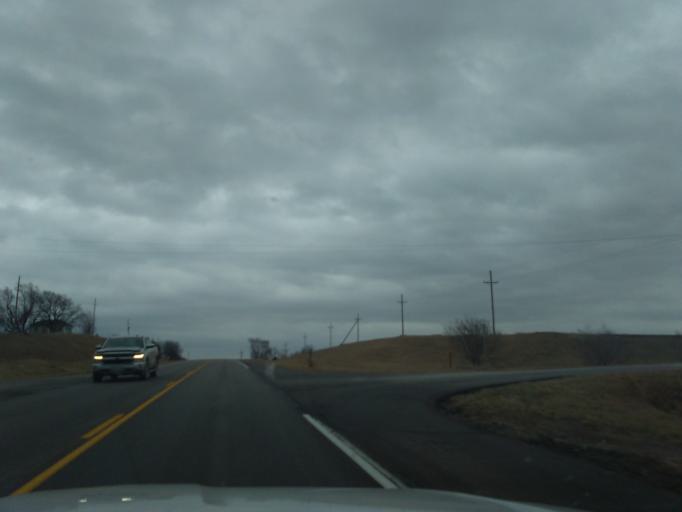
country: US
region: Nebraska
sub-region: Nemaha County
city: Auburn
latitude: 40.3927
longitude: -95.7821
